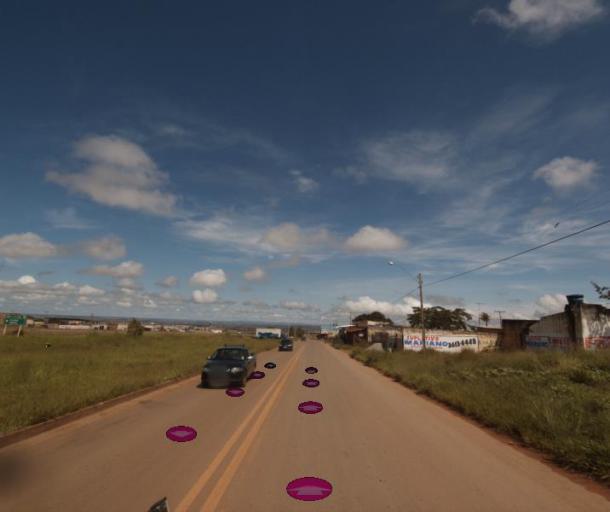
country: BR
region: Federal District
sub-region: Brasilia
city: Brasilia
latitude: -15.7372
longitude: -48.2935
